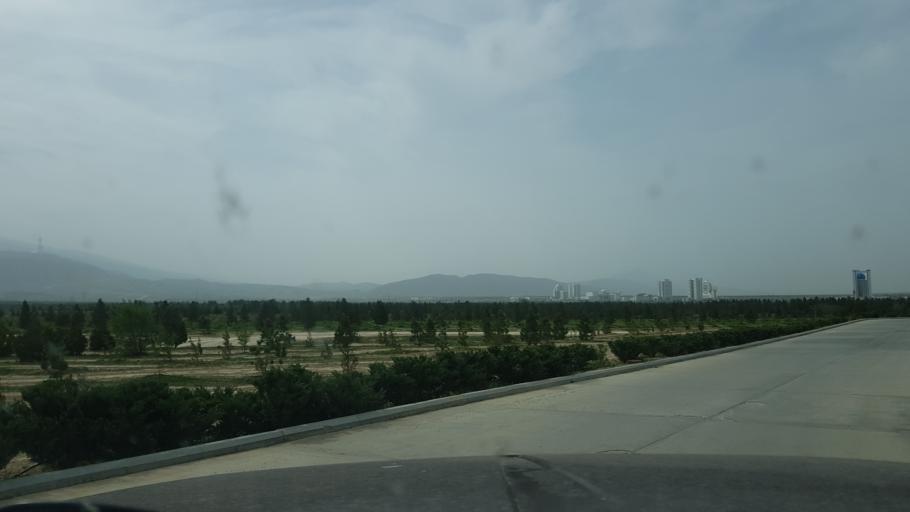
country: TM
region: Ahal
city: Ashgabat
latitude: 37.8816
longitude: 58.3303
